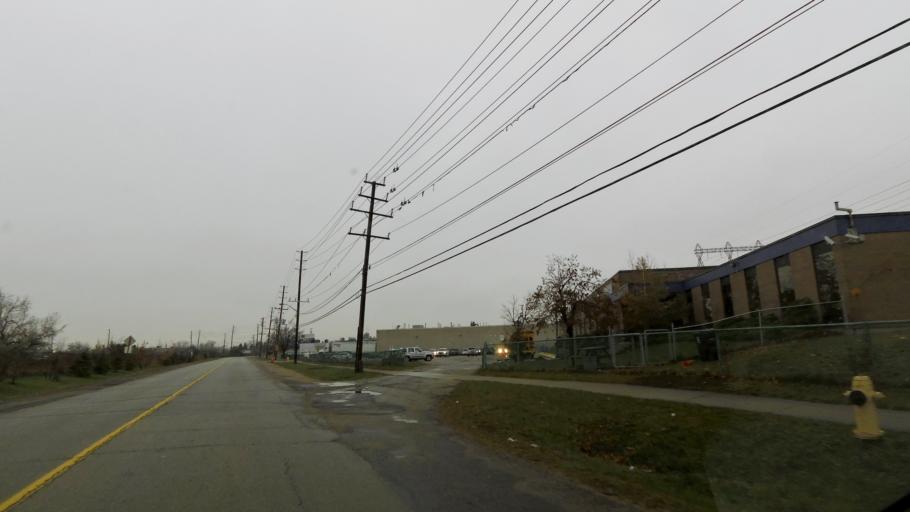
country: CA
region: Ontario
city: Etobicoke
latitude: 43.6908
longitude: -79.5809
